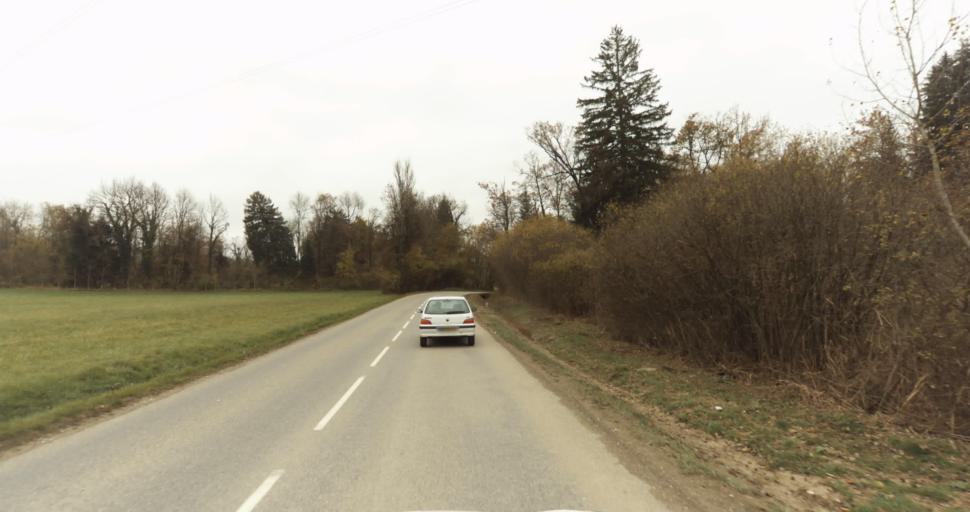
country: FR
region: Rhone-Alpes
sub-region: Departement de la Haute-Savoie
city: Viuz-la-Chiesaz
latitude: 45.8483
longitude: 6.0672
